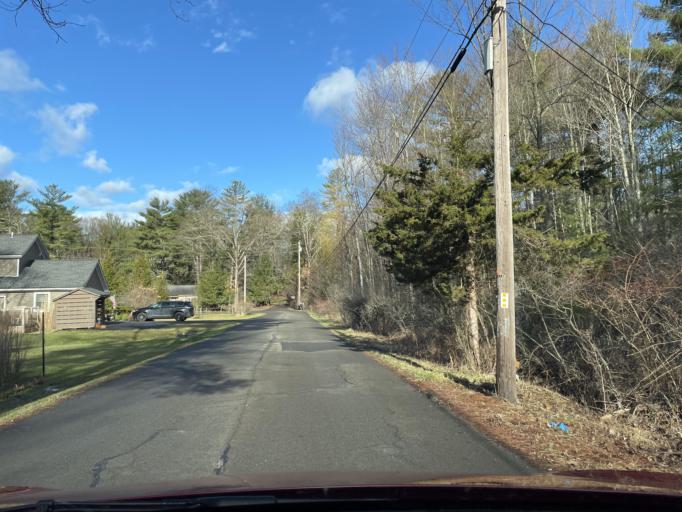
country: US
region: New York
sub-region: Ulster County
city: Woodstock
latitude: 42.0429
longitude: -74.1231
